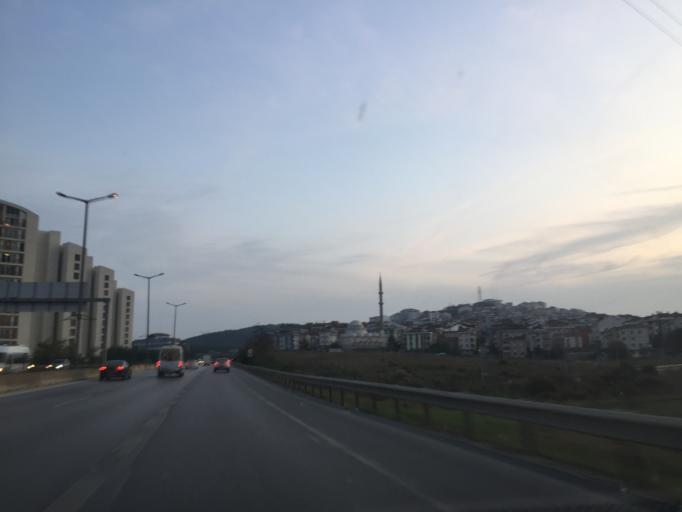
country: TR
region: Istanbul
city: Samandira
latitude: 40.9657
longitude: 29.2191
